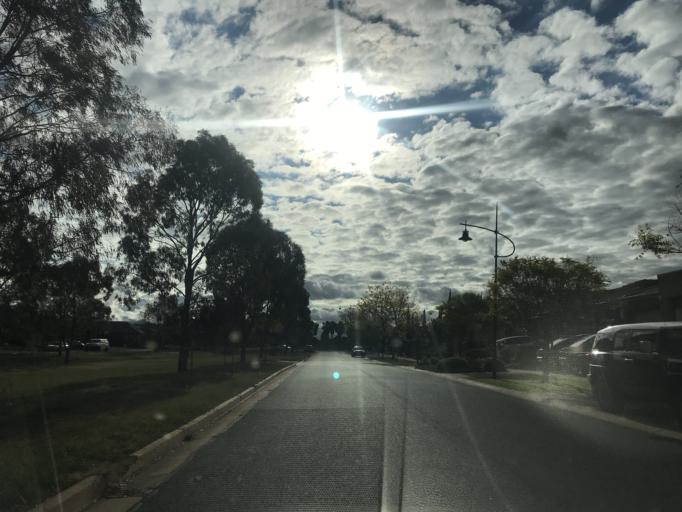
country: AU
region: Victoria
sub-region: Wyndham
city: Point Cook
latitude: -37.8943
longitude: 144.7362
